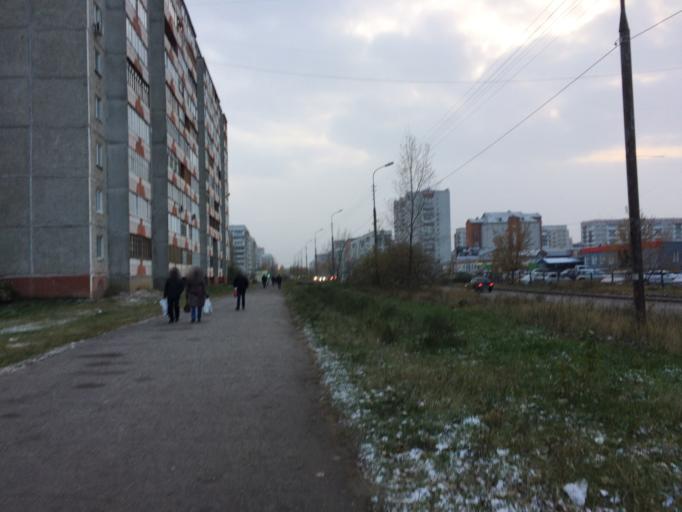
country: RU
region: Mariy-El
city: Yoshkar-Ola
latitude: 56.6378
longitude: 47.9232
